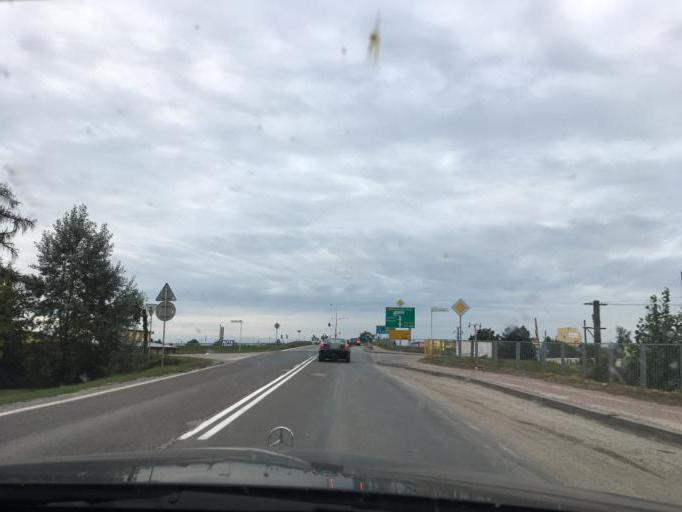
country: PL
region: Masovian Voivodeship
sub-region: Powiat ostrowski
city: Ostrow Mazowiecka
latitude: 52.8204
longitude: 21.8882
